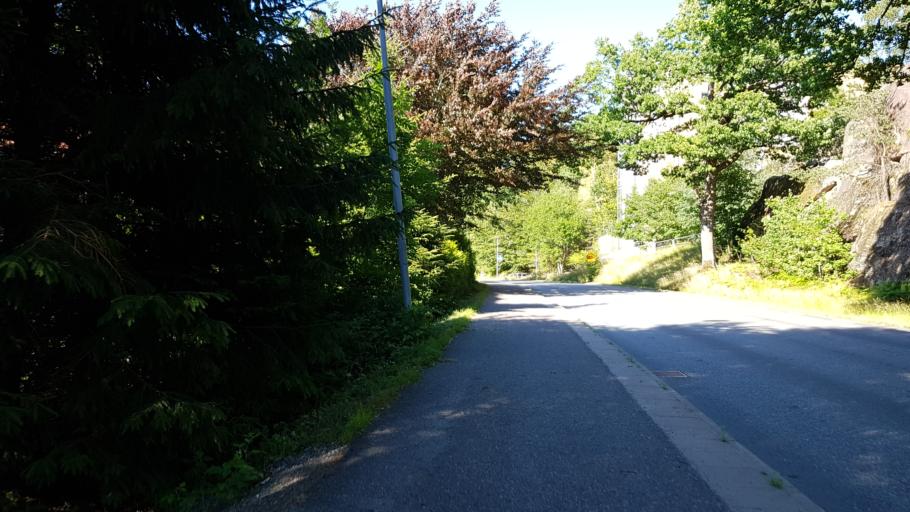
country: SE
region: Vaestra Goetaland
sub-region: Harryda Kommun
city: Molnlycke
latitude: 57.6506
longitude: 12.1272
